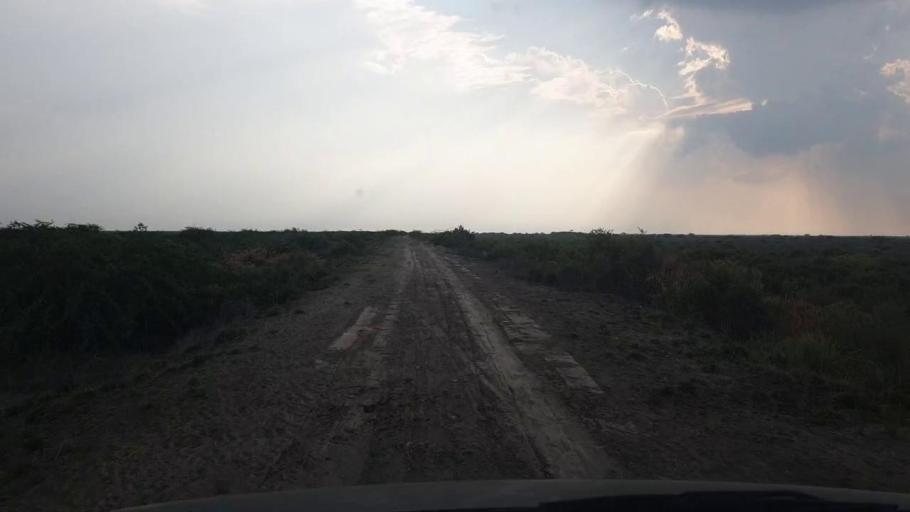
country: PK
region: Sindh
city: Badin
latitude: 24.4728
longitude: 68.6982
